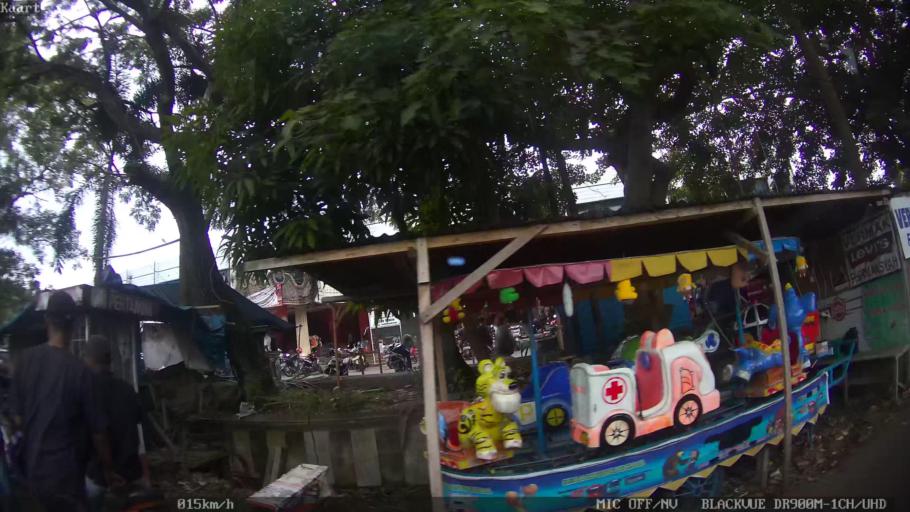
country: ID
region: Lampung
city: Bandarlampung
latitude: -5.4102
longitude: 105.2475
